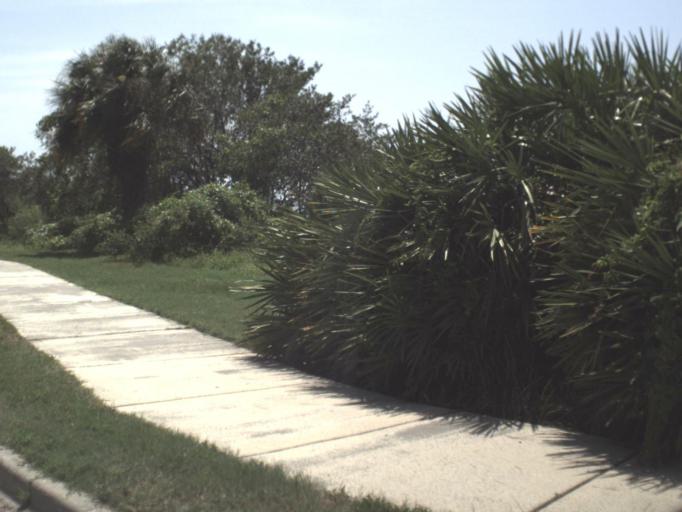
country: US
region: Florida
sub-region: Pinellas County
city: Dunedin
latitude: 28.0037
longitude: -82.7927
